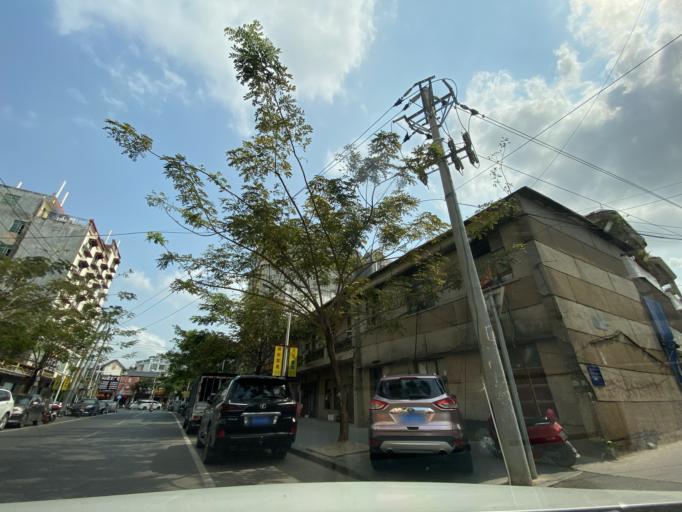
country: CN
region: Hainan
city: Yingzhou
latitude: 18.4216
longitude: 109.8504
